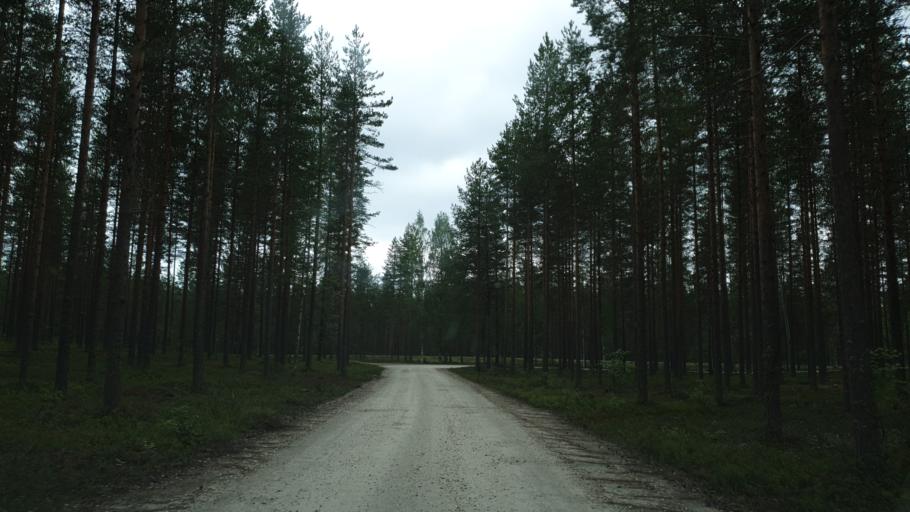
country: FI
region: Kainuu
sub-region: Kehys-Kainuu
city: Kuhmo
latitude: 64.1917
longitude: 29.1968
